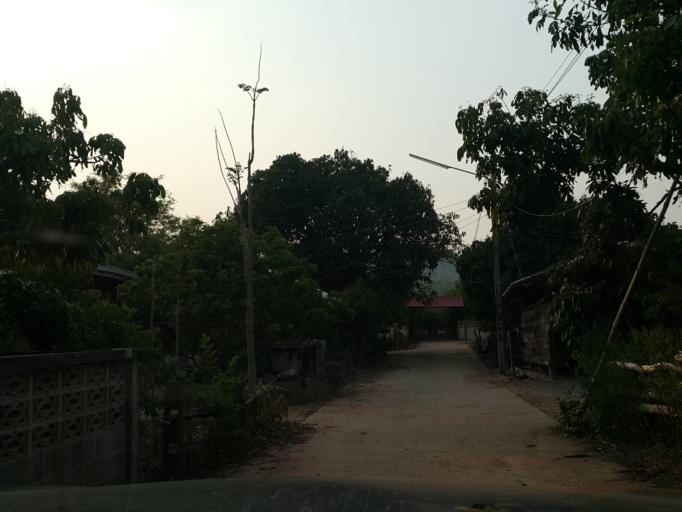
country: TH
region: Lamphun
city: Li
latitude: 17.8640
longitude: 99.0313
